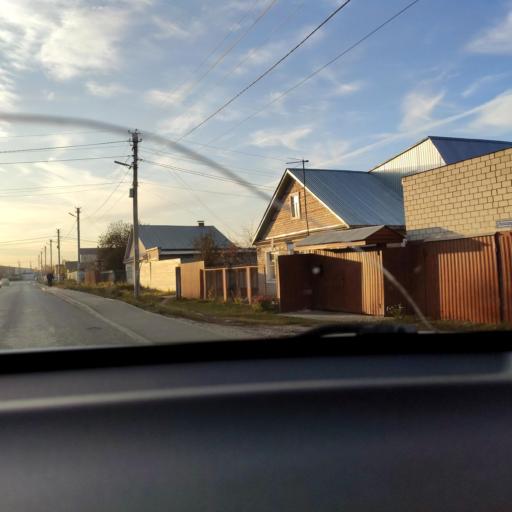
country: RU
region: Tatarstan
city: Staroye Arakchino
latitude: 55.8792
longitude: 49.0460
